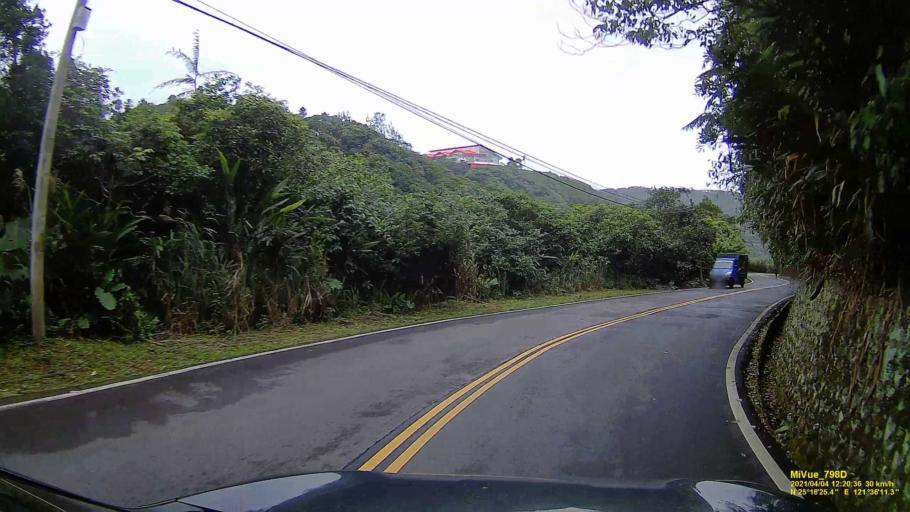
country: TW
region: Taiwan
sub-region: Keelung
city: Keelung
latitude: 25.2738
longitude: 121.6032
